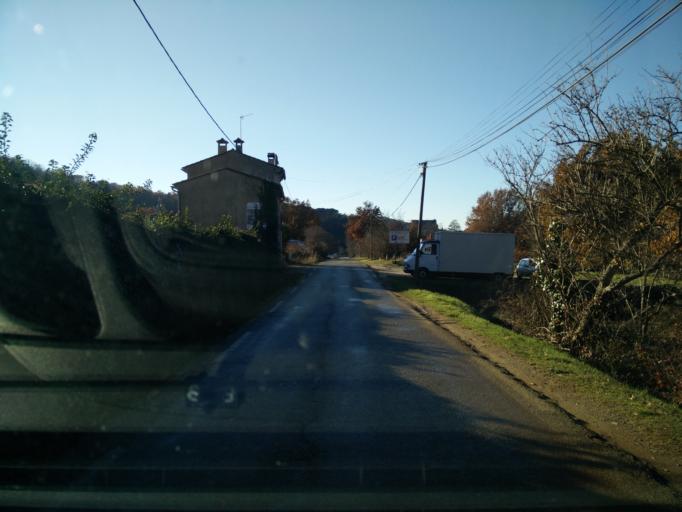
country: FR
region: Provence-Alpes-Cote d'Azur
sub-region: Departement du Var
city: Collobrieres
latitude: 43.2377
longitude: 6.3185
